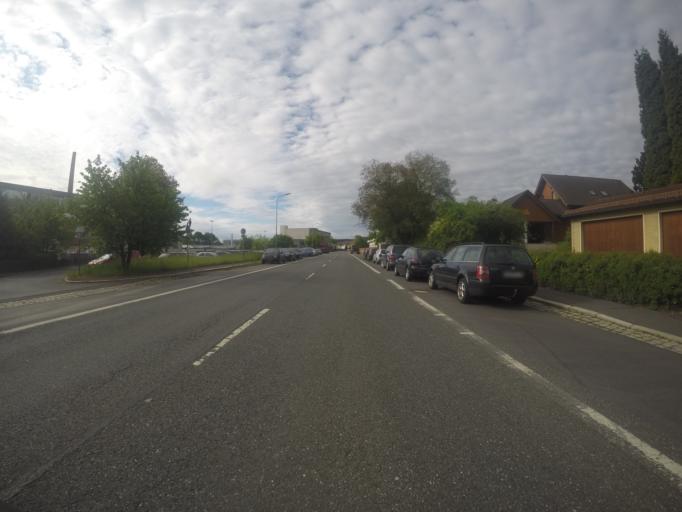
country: DE
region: Bavaria
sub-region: Upper Franconia
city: Schonwald
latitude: 50.2044
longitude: 12.0944
